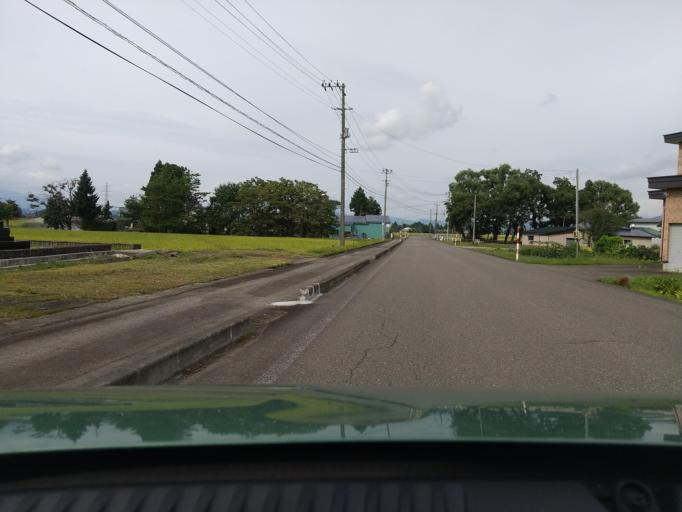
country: JP
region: Akita
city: Kakunodatemachi
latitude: 39.5507
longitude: 140.5680
